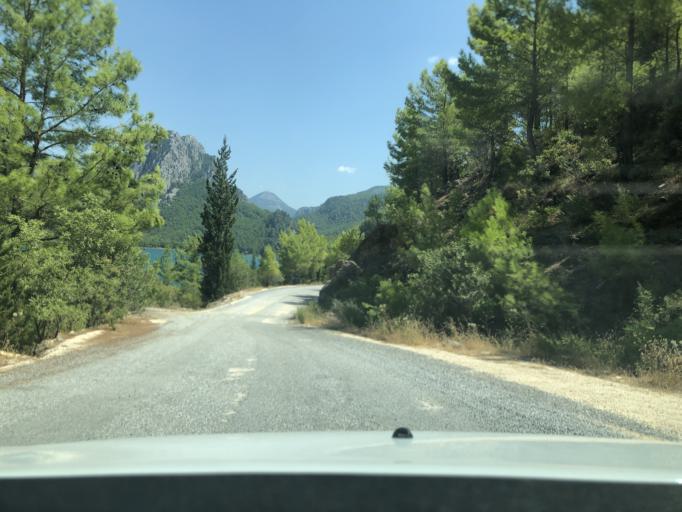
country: TR
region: Antalya
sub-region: Manavgat
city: Manavgat
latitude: 36.9086
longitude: 31.5527
